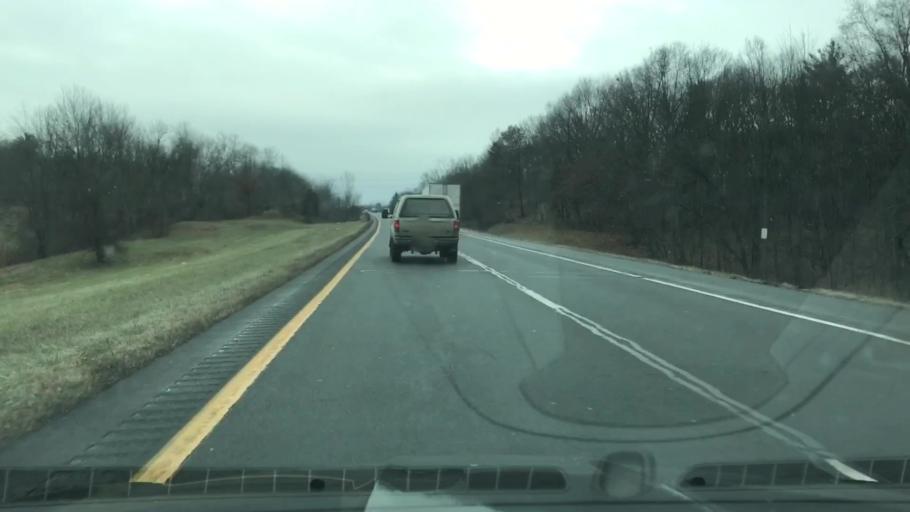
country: US
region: New York
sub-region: Orange County
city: Walden
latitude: 41.5178
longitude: -74.1756
